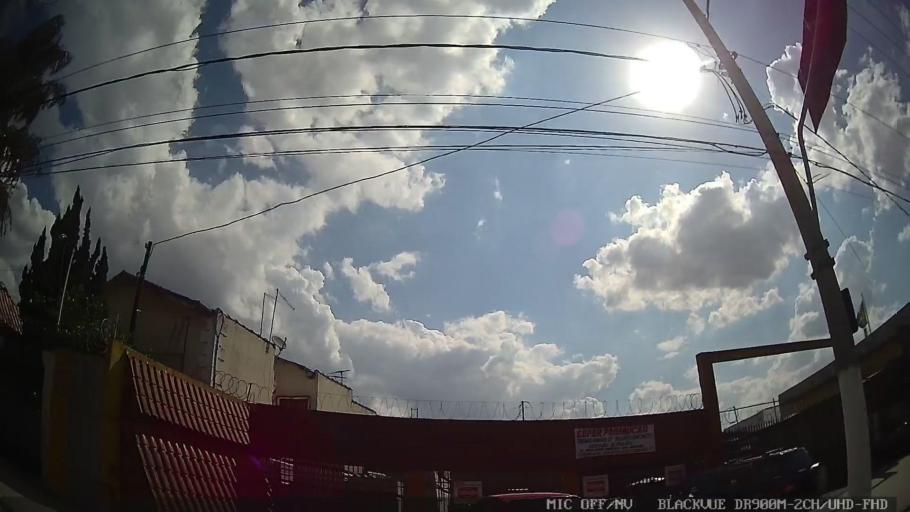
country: BR
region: Sao Paulo
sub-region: Ferraz De Vasconcelos
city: Ferraz de Vasconcelos
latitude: -23.5107
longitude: -46.4291
